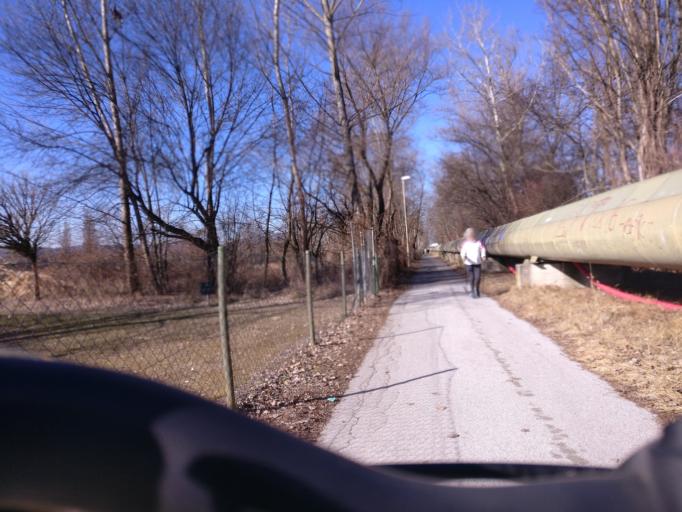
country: AT
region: Styria
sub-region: Politischer Bezirk Graz-Umgebung
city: Feldkirchen bei Graz
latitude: 47.0331
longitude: 15.4485
